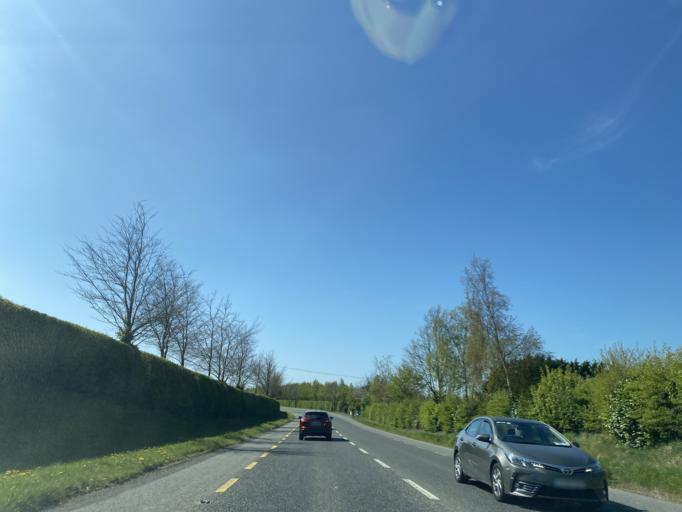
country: IE
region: Leinster
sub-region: Kildare
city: Maynooth
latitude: 53.3346
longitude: -6.6058
